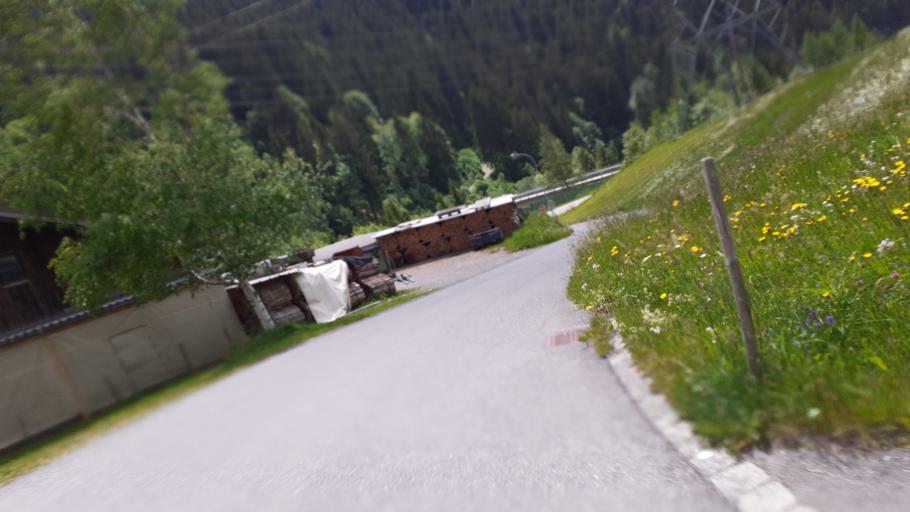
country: AT
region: Vorarlberg
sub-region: Politischer Bezirk Bludenz
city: Dalaas
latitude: 47.1284
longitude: 10.0292
